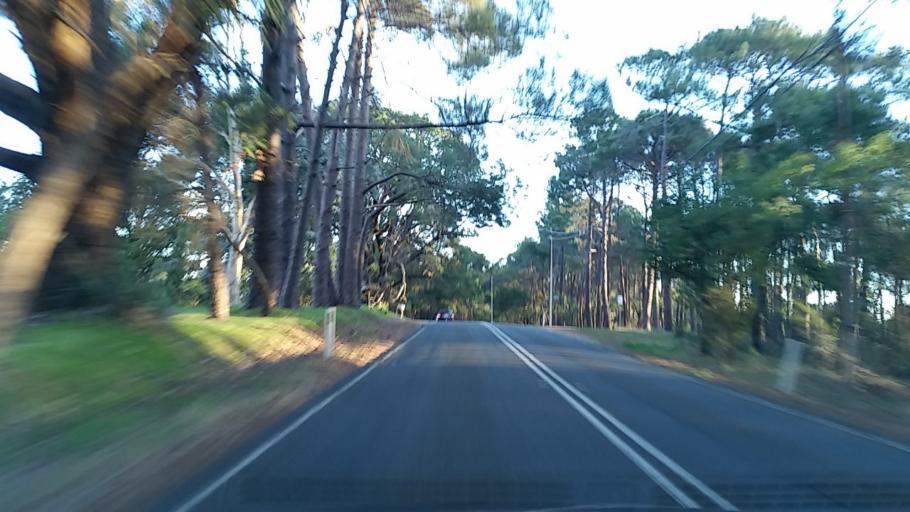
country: AU
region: South Australia
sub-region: Adelaide Hills
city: Upper Sturt
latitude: -35.0622
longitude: 138.6768
